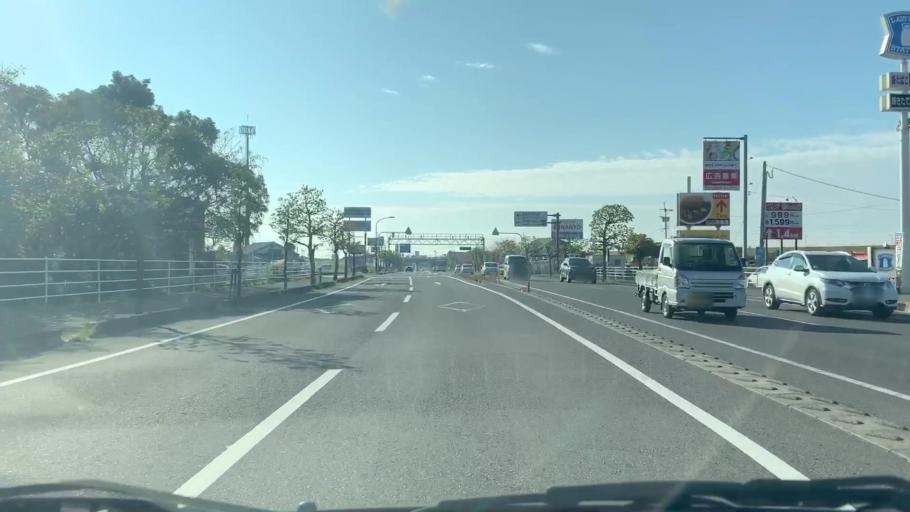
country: JP
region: Saga Prefecture
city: Saga-shi
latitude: 33.3130
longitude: 130.2758
